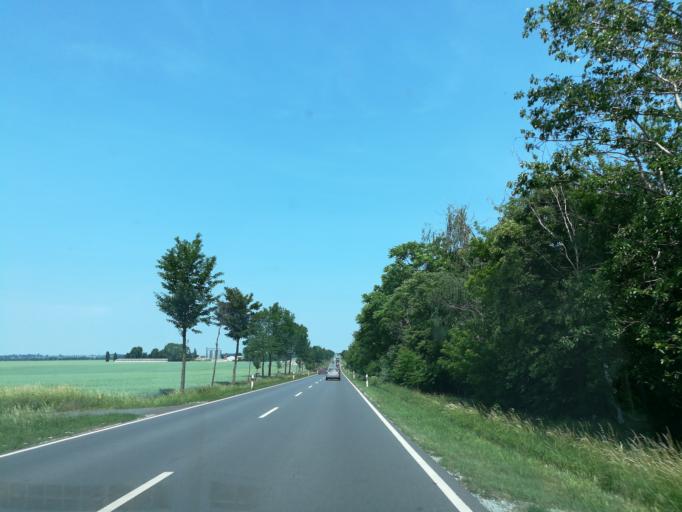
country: DE
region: Saxony-Anhalt
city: Aschersleben
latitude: 51.7908
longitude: 11.4591
